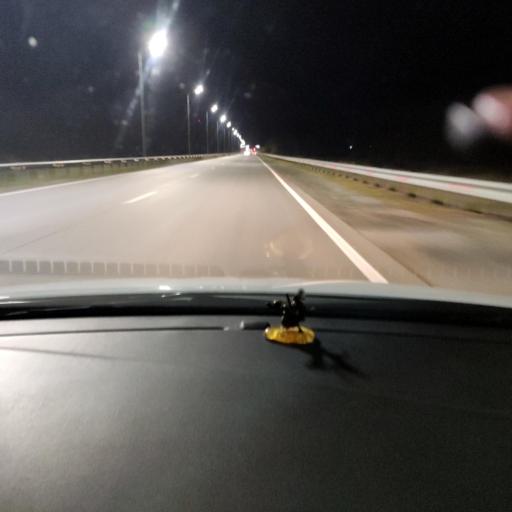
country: RU
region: Tatarstan
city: Stolbishchi
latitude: 55.6469
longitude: 49.1280
